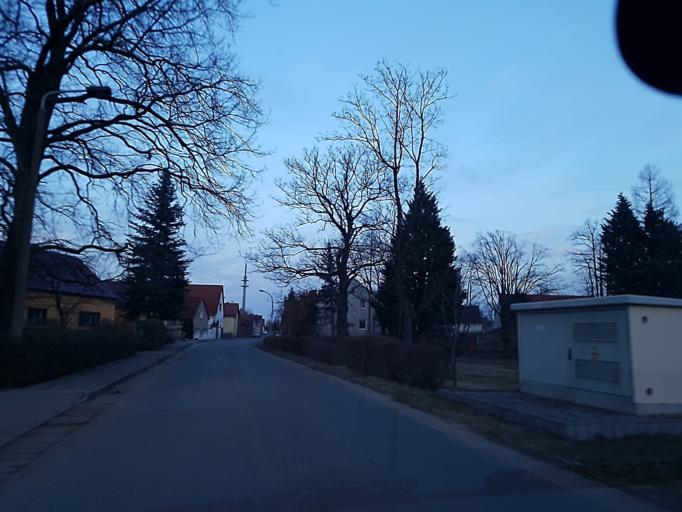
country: DE
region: Brandenburg
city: Herzberg
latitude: 51.6909
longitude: 13.2471
